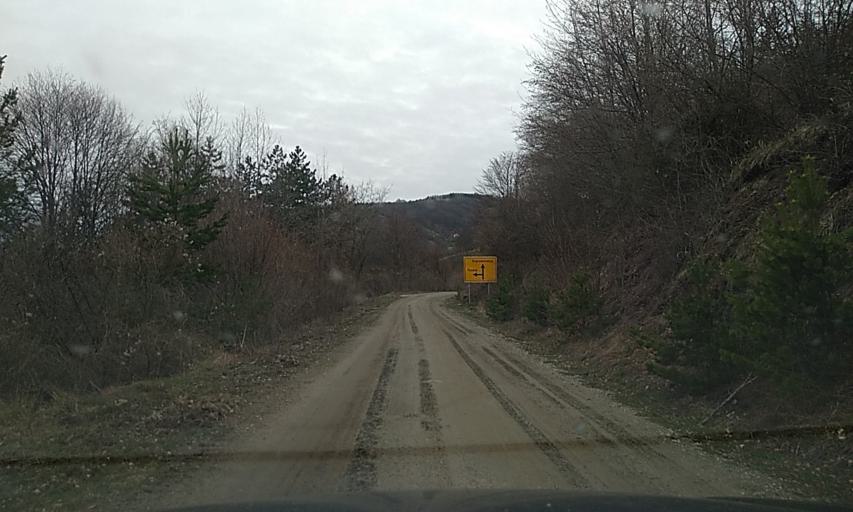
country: MK
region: Kriva Palanka
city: Kriva Palanka
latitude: 42.3429
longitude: 22.3518
